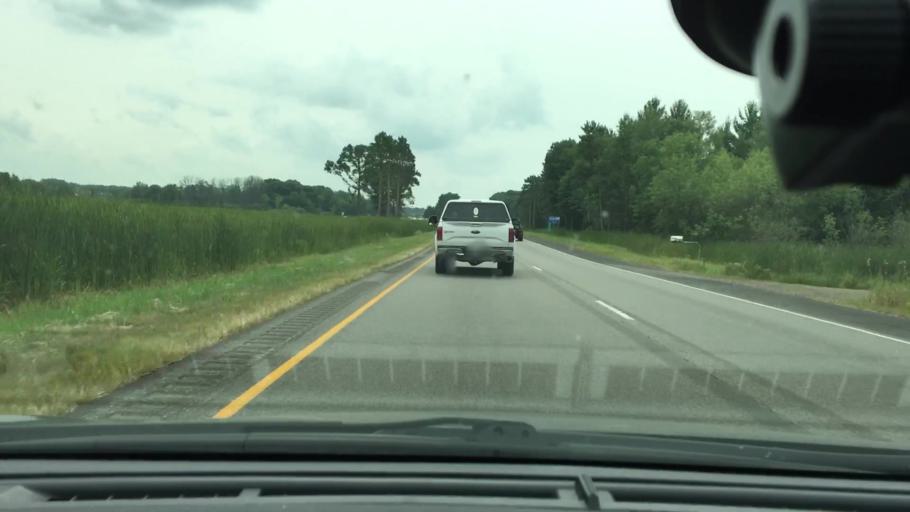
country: US
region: Minnesota
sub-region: Mille Lacs County
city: Princeton
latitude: 45.5138
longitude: -93.5831
